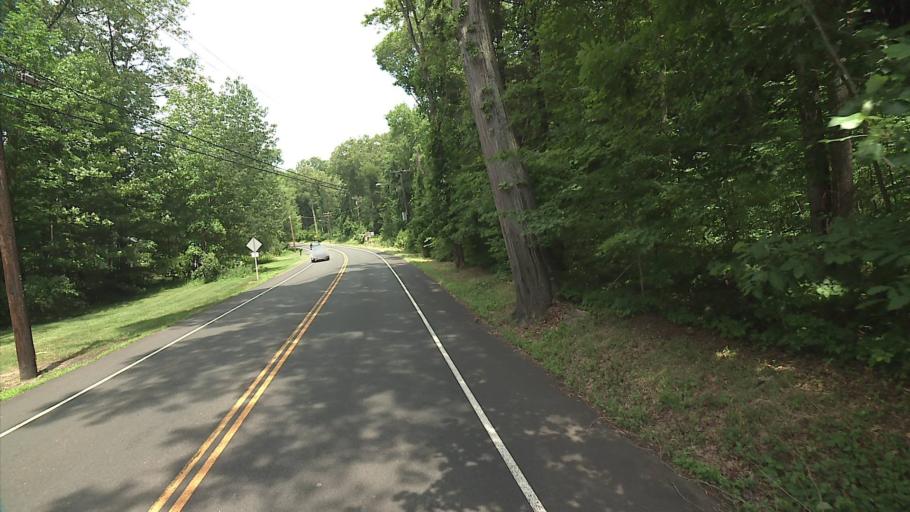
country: US
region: Connecticut
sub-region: New Haven County
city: North Branford
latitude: 41.3174
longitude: -72.7514
